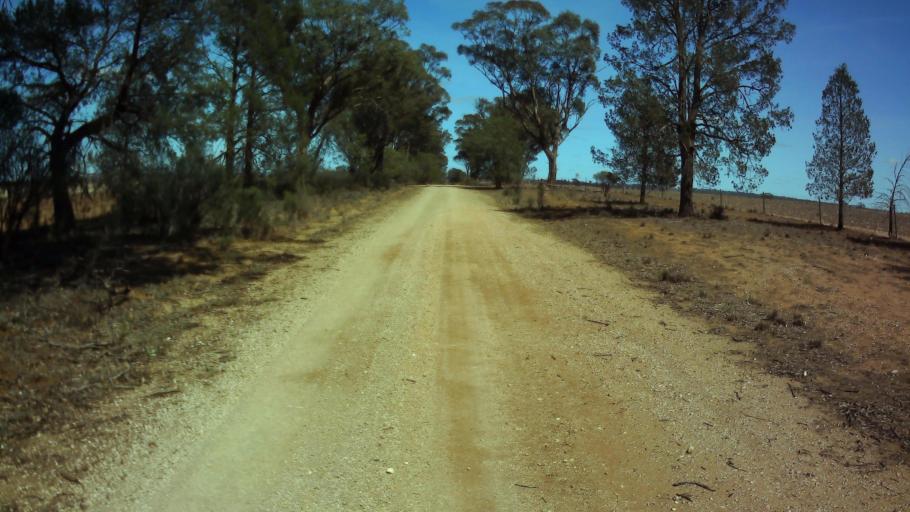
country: AU
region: New South Wales
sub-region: Weddin
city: Grenfell
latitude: -33.7269
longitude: 147.8809
